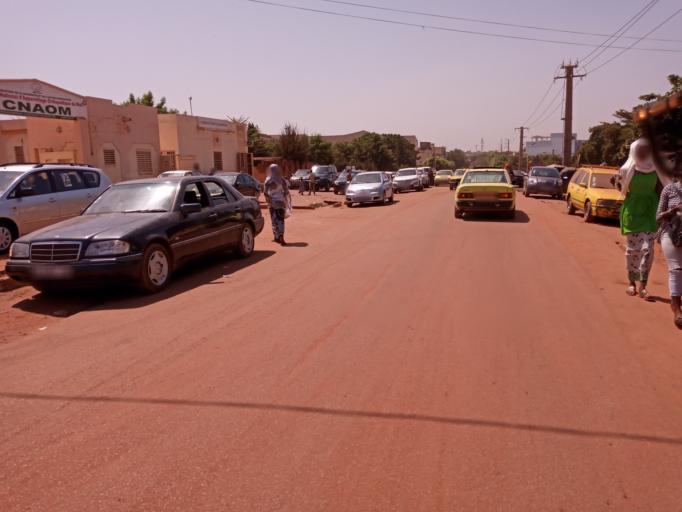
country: ML
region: Bamako
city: Bamako
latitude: 12.6116
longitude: -7.9959
